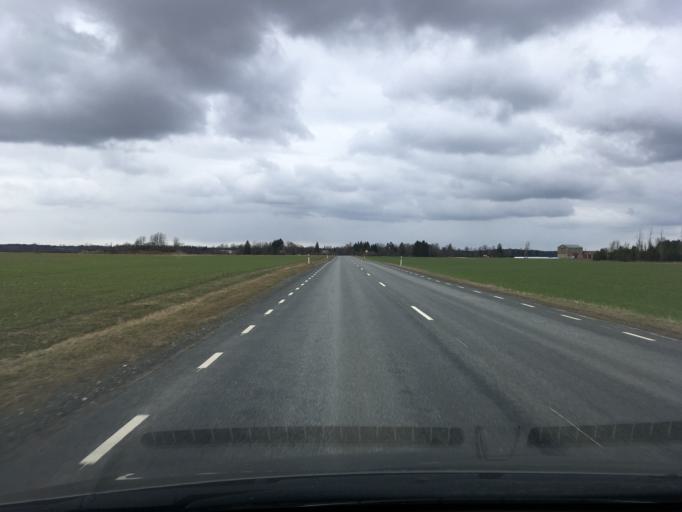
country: EE
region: Laeaene
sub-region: Lihula vald
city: Lihula
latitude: 58.5758
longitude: 23.9822
